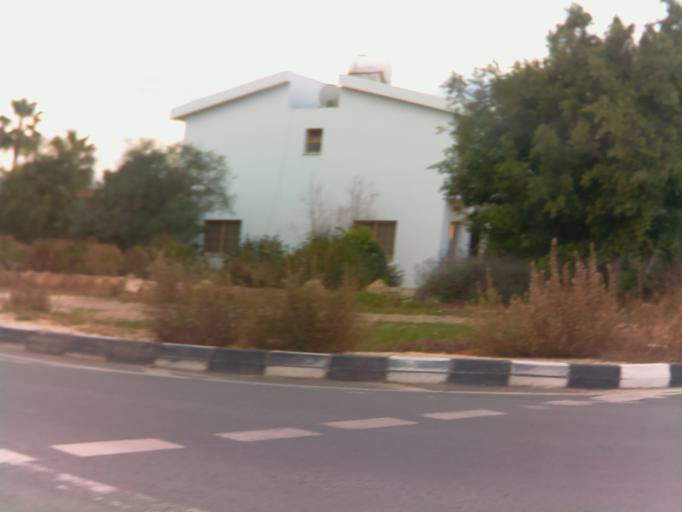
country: CY
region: Pafos
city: Pegeia
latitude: 34.8574
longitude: 32.3770
